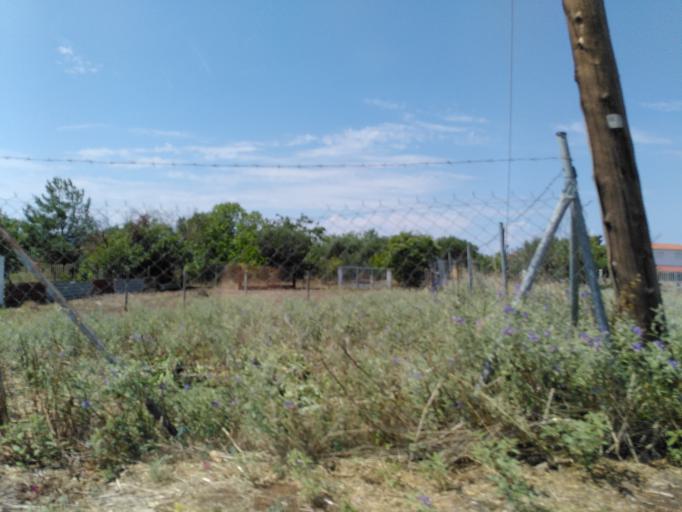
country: GR
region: Central Macedonia
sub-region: Nomos Thessalonikis
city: Nea Michaniona
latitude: 40.4420
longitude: 22.8684
